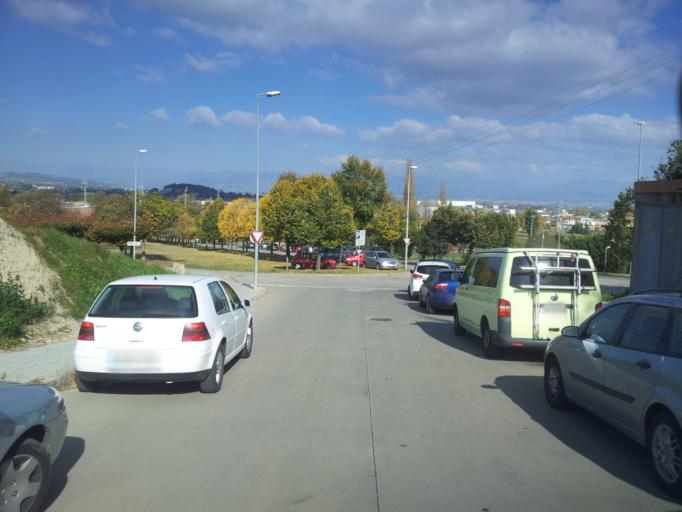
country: ES
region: Catalonia
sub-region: Provincia de Barcelona
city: Vic
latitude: 41.9339
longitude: 2.2382
